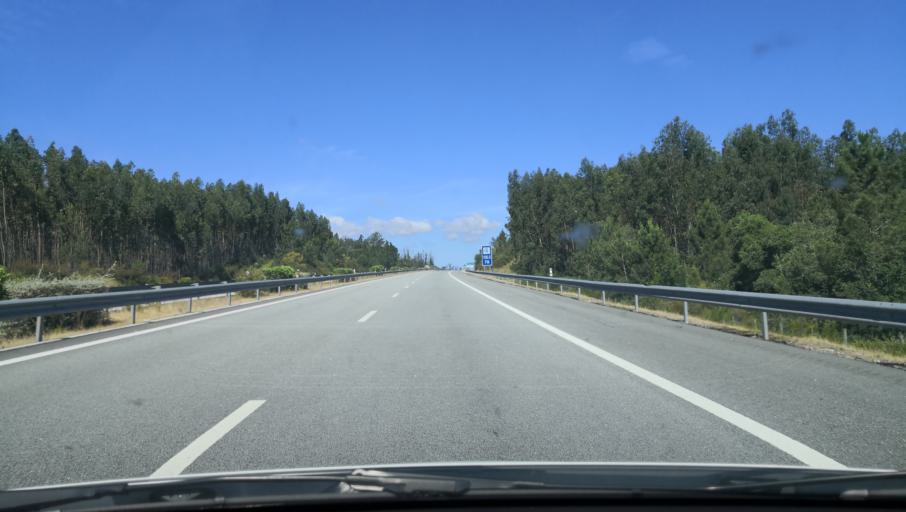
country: PT
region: Coimbra
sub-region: Cantanhede
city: Cantanhede
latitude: 40.2840
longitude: -8.5430
